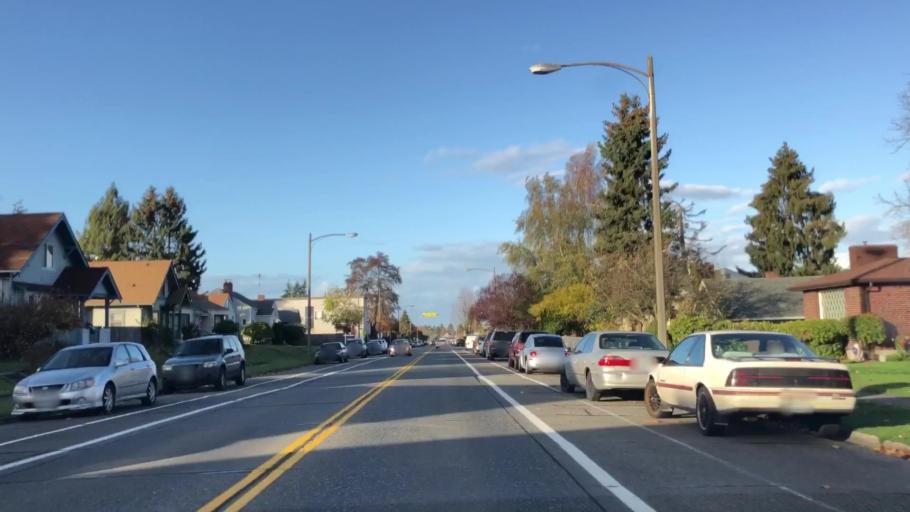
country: US
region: Washington
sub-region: Pierce County
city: Tacoma
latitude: 47.2088
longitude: -122.4431
